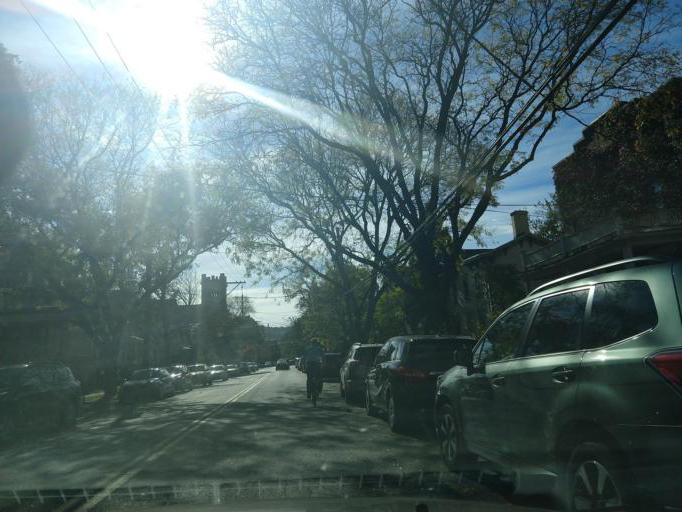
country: US
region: New York
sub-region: Tompkins County
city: Ithaca
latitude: 42.4437
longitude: -76.4992
